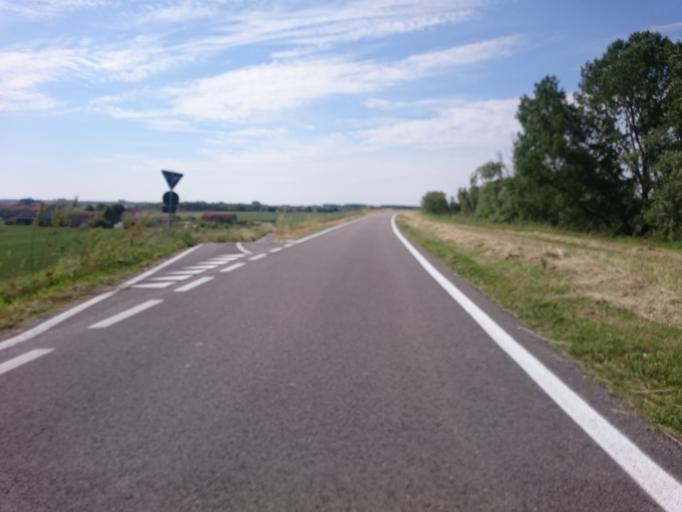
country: IT
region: Veneto
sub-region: Provincia di Rovigo
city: Corbola
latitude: 44.9885
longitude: 12.0898
